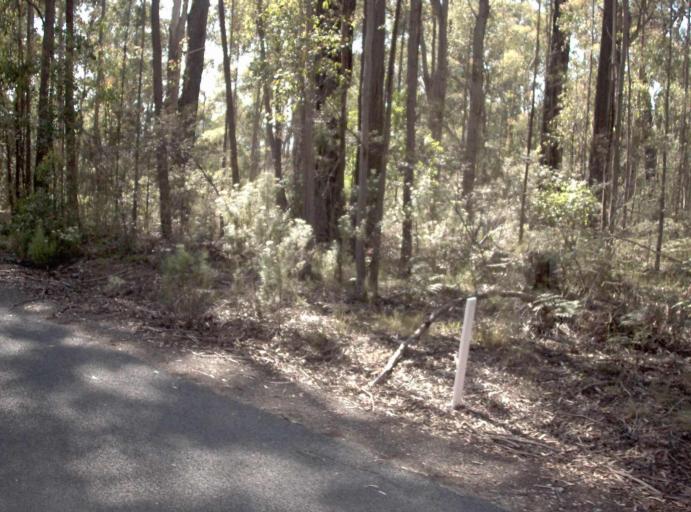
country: AU
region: New South Wales
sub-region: Bombala
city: Bombala
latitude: -37.3871
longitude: 148.6241
